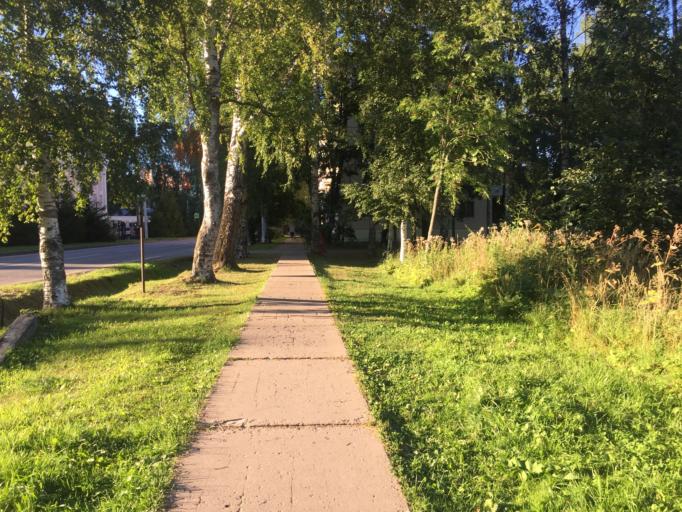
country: RU
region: Leningrad
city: Murino
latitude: 60.0378
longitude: 30.4653
